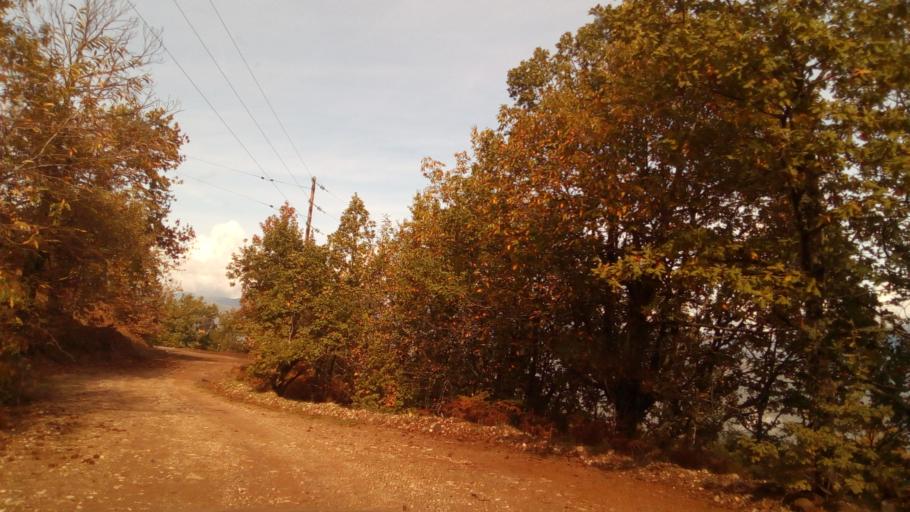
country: GR
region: West Greece
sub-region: Nomos Achaias
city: Kamarai
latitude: 38.4750
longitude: 22.0219
